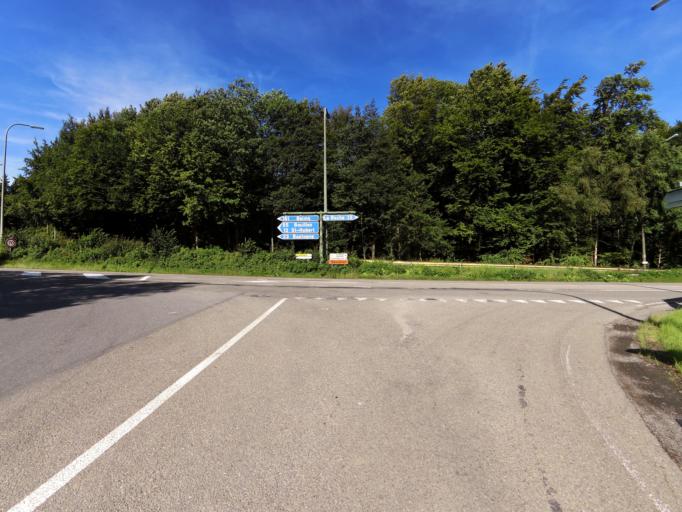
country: BE
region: Wallonia
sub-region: Province du Luxembourg
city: Tenneville
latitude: 50.1085
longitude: 5.4748
